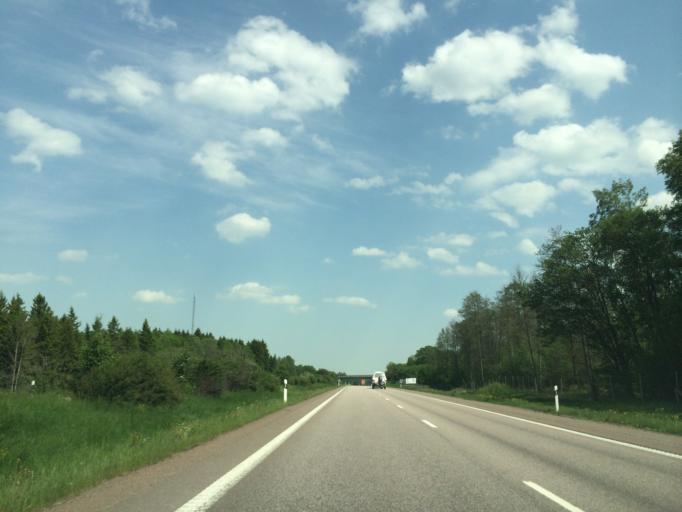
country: SE
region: OEstergoetland
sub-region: Mjolby Kommun
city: Mjolby
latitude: 58.3087
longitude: 15.0108
